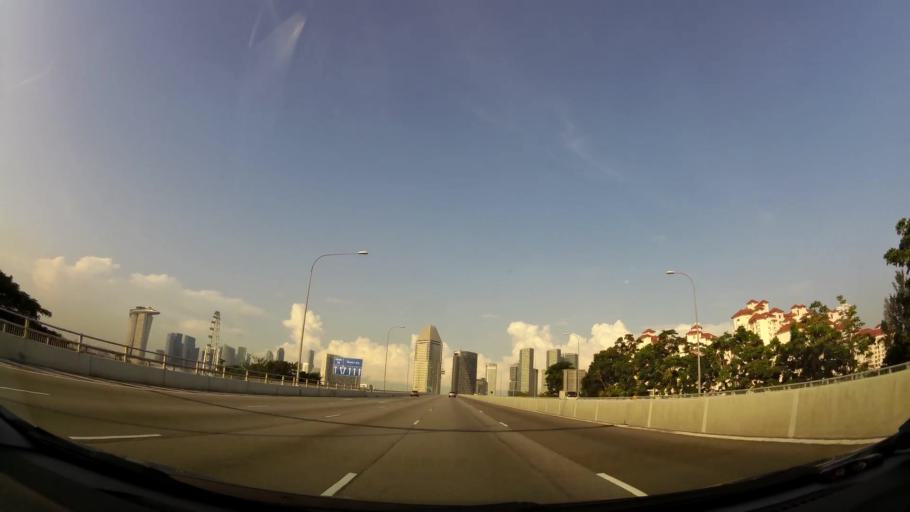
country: SG
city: Singapore
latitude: 1.2949
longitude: 103.8693
